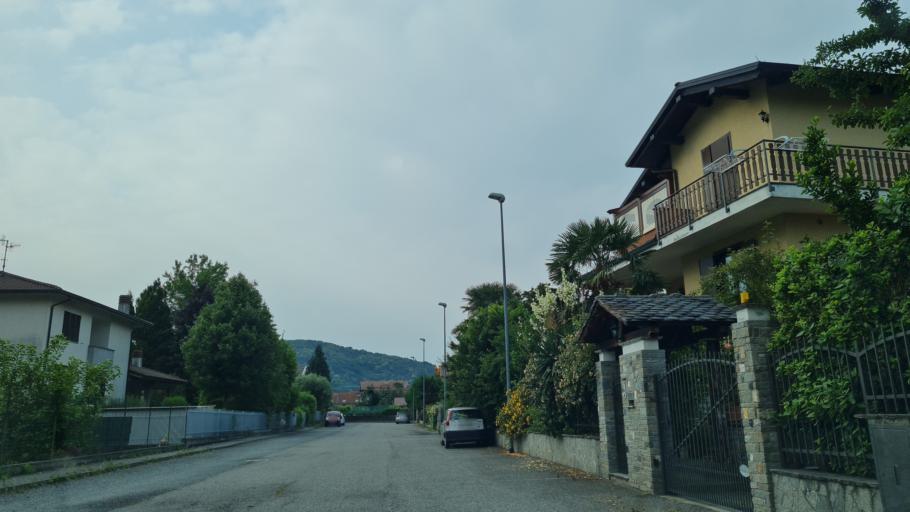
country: IT
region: Piedmont
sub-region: Provincia di Torino
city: Borgofranco d'Ivrea
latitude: 45.5139
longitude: 7.8612
